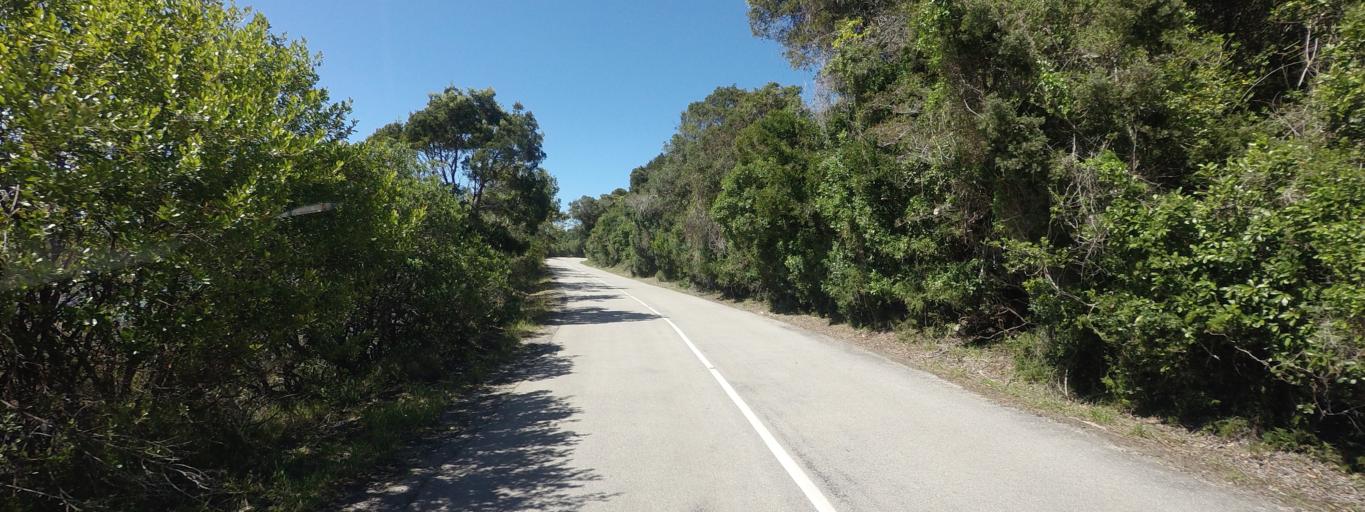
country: ZA
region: Western Cape
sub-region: Eden District Municipality
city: Plettenberg Bay
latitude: -33.9739
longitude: 23.5617
